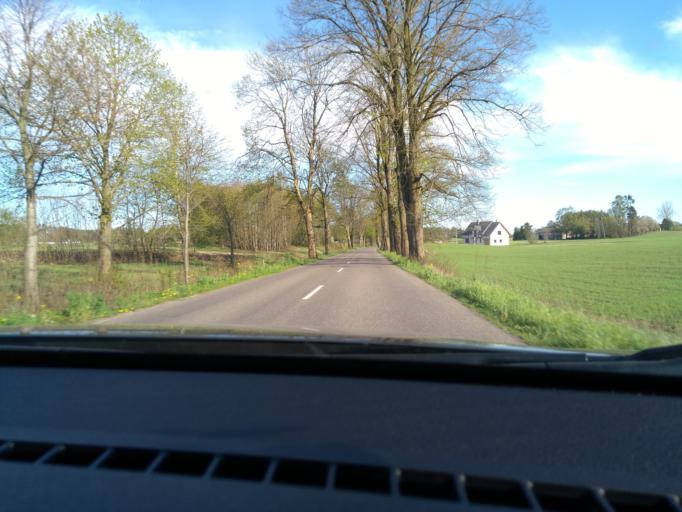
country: PL
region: Pomeranian Voivodeship
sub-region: Powiat kartuski
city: Suleczyno
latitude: 54.3346
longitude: 17.7679
